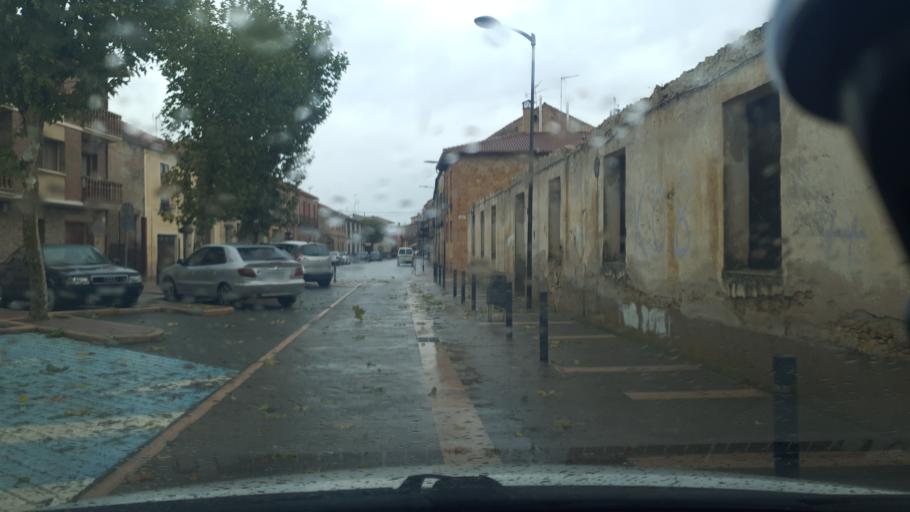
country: ES
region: Castille and Leon
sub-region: Provincia de Segovia
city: Carbonero el Mayor
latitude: 41.1200
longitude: -4.2647
